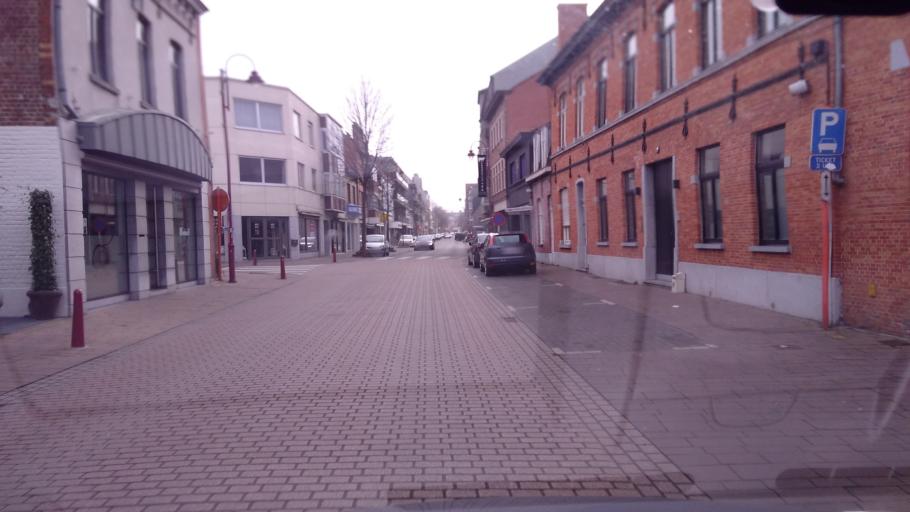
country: BE
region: Flanders
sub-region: Provincie Oost-Vlaanderen
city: Aalter
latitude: 51.0911
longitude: 3.4468
